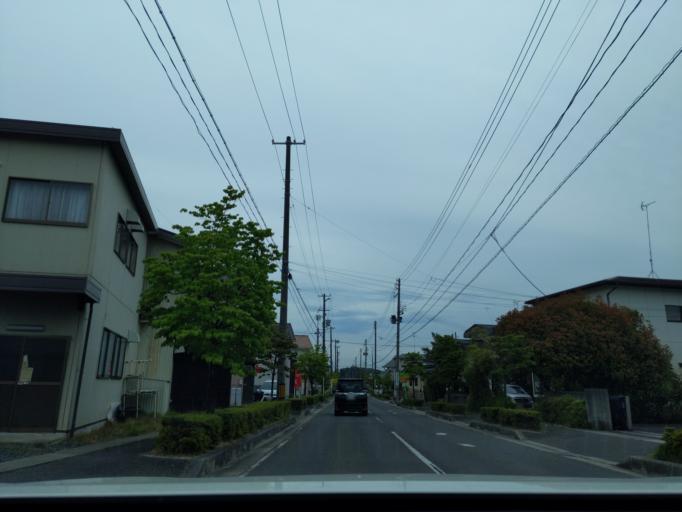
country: JP
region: Fukushima
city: Koriyama
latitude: 37.3749
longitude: 140.3657
